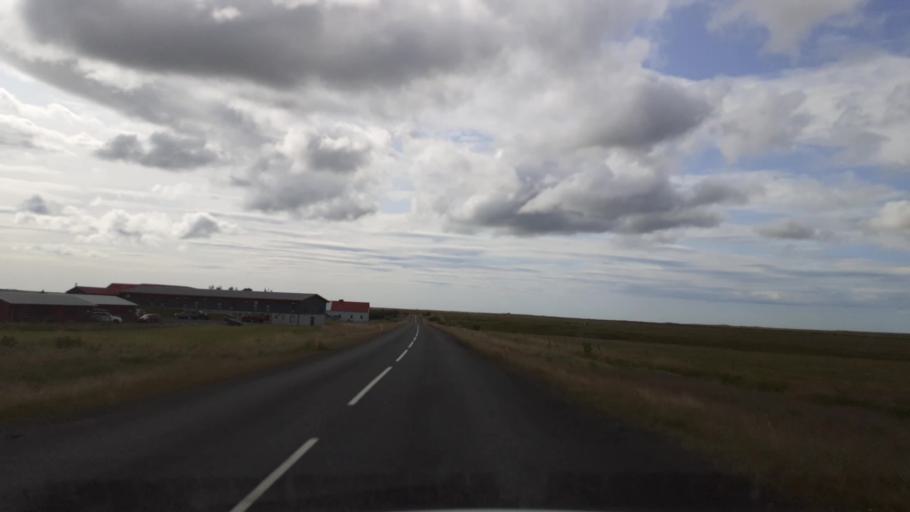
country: IS
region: South
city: Vestmannaeyjar
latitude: 63.8329
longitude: -20.4212
